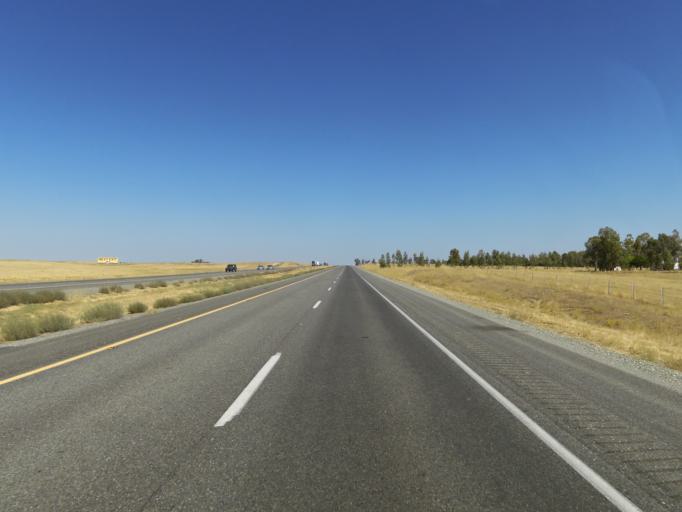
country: US
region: California
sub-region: Tehama County
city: Corning
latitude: 39.8587
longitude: -122.1999
